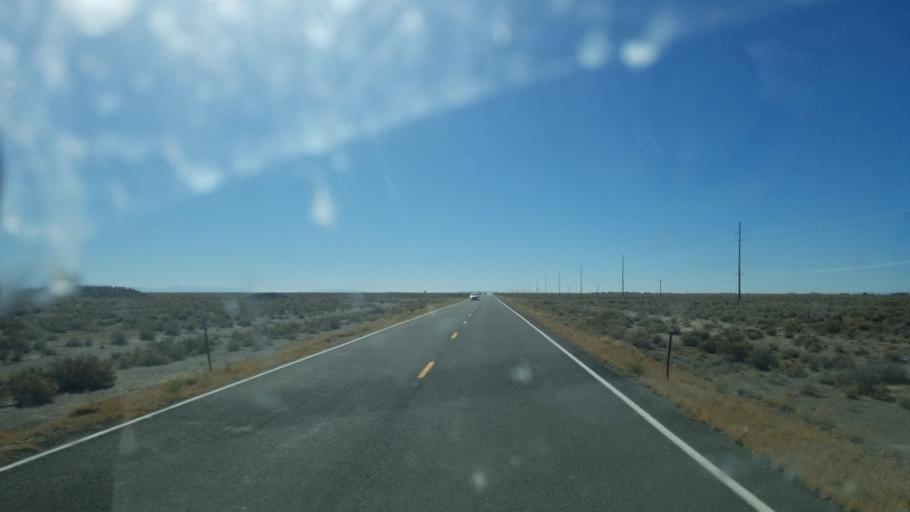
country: US
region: Colorado
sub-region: Saguache County
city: Center
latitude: 37.8782
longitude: -105.8950
